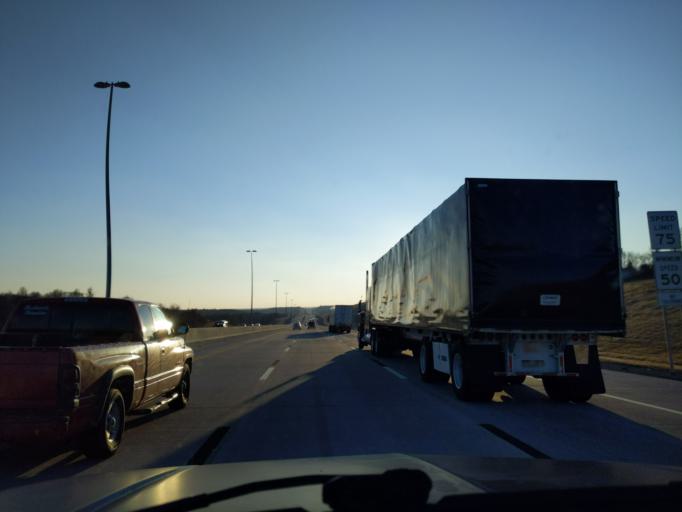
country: US
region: Oklahoma
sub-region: Creek County
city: Kellyville
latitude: 35.9809
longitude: -96.2033
